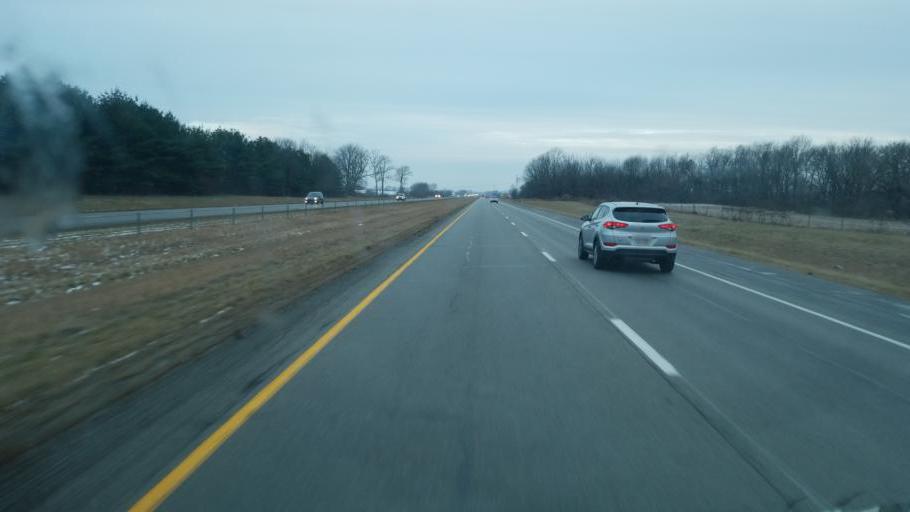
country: US
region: Indiana
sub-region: Hancock County
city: Greenfield
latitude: 39.8259
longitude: -85.6611
